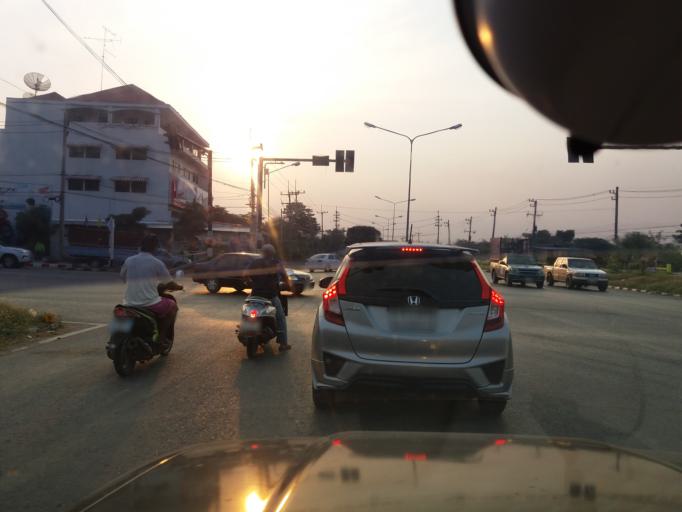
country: TH
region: Sing Buri
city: Sing Buri
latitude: 14.8860
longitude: 100.3908
